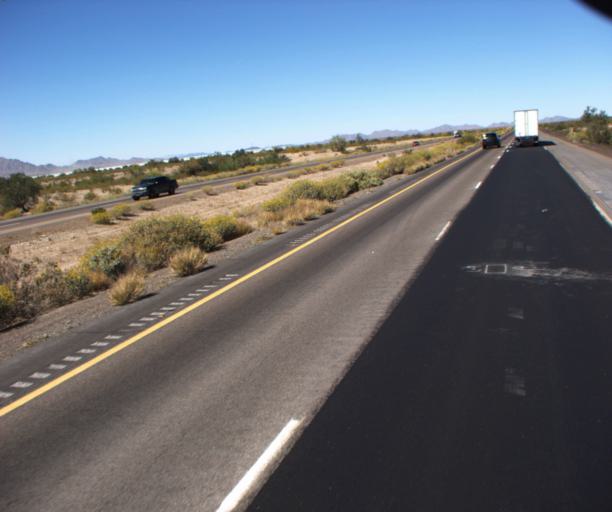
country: US
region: Arizona
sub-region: Maricopa County
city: Gila Bend
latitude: 33.0640
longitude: -112.6450
